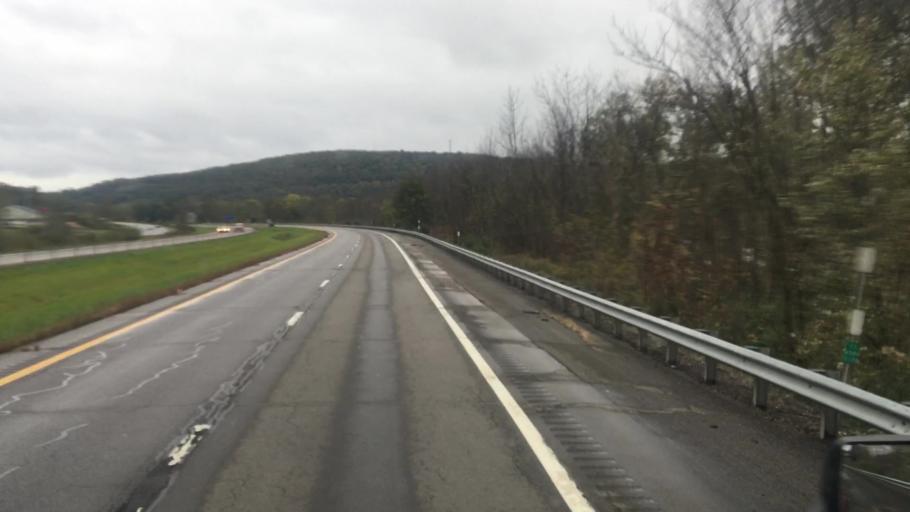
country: US
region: New York
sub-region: Tioga County
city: Owego
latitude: 42.0965
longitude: -76.2372
